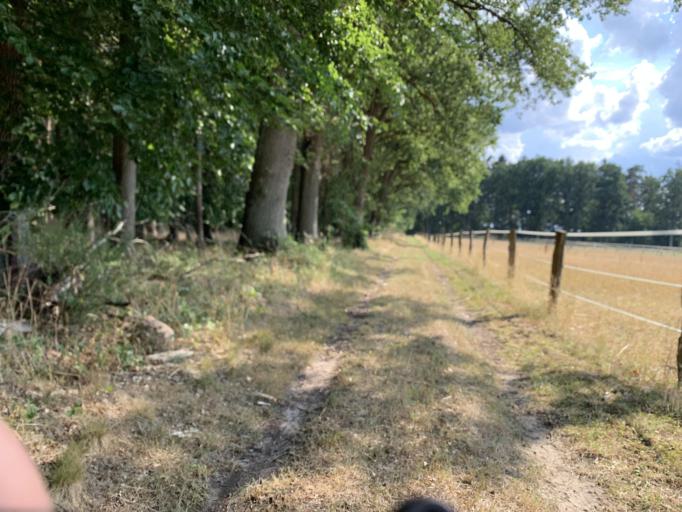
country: DE
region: Lower Saxony
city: Thomasburg
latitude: 53.2415
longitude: 10.6390
